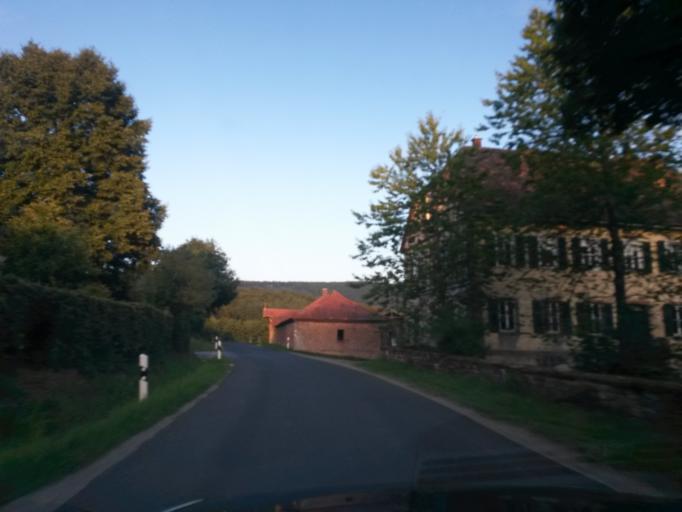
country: DE
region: Bavaria
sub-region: Regierungsbezirk Unterfranken
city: Rechtenbach
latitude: 49.9455
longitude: 9.4784
